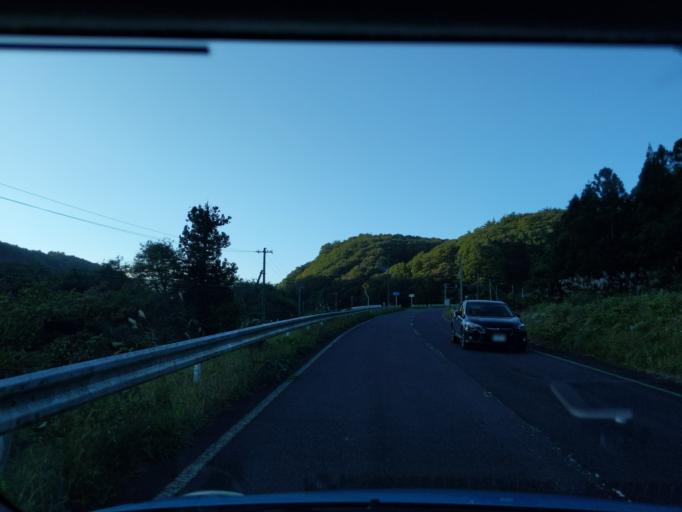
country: JP
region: Iwate
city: Ichinoseki
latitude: 39.0231
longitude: 141.0197
